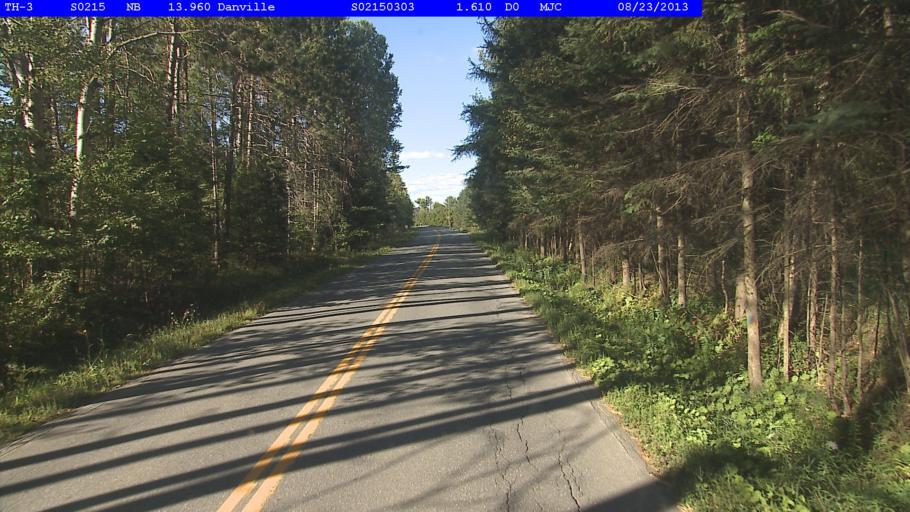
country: US
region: Vermont
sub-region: Caledonia County
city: Saint Johnsbury
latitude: 44.3882
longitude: -72.1422
